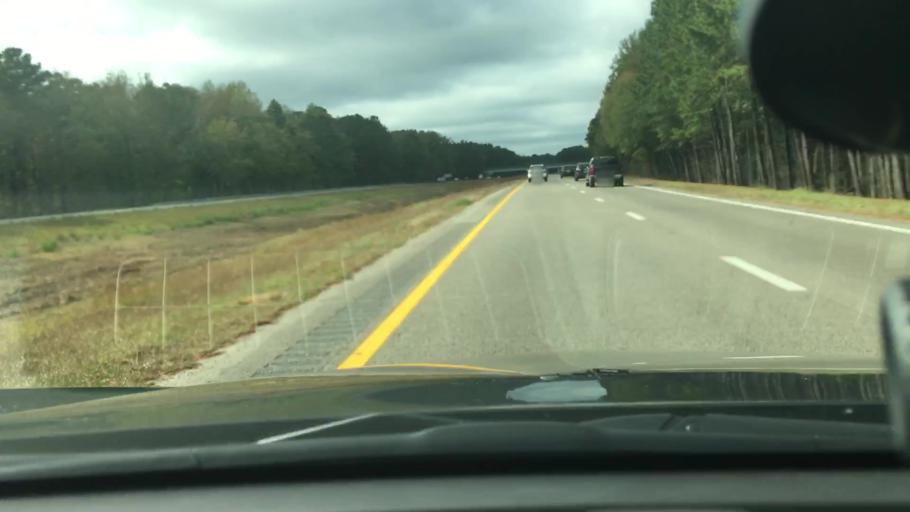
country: US
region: North Carolina
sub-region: Nash County
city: Spring Hope
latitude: 35.7886
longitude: -78.1309
